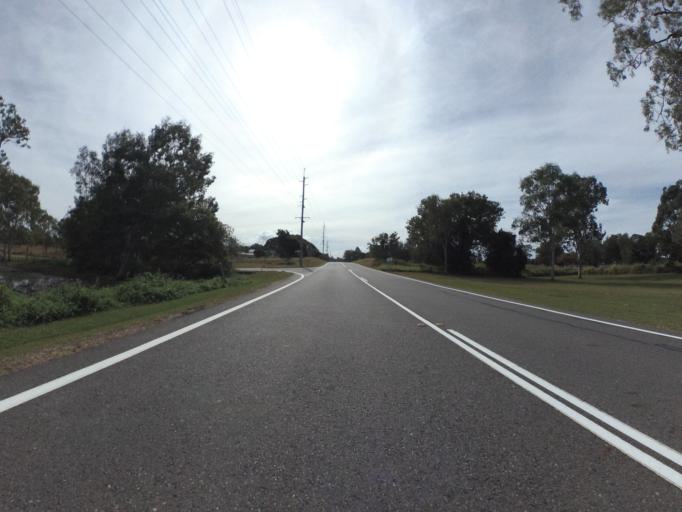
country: AU
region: Queensland
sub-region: Brisbane
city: Moggill
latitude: -27.5863
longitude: 152.8612
